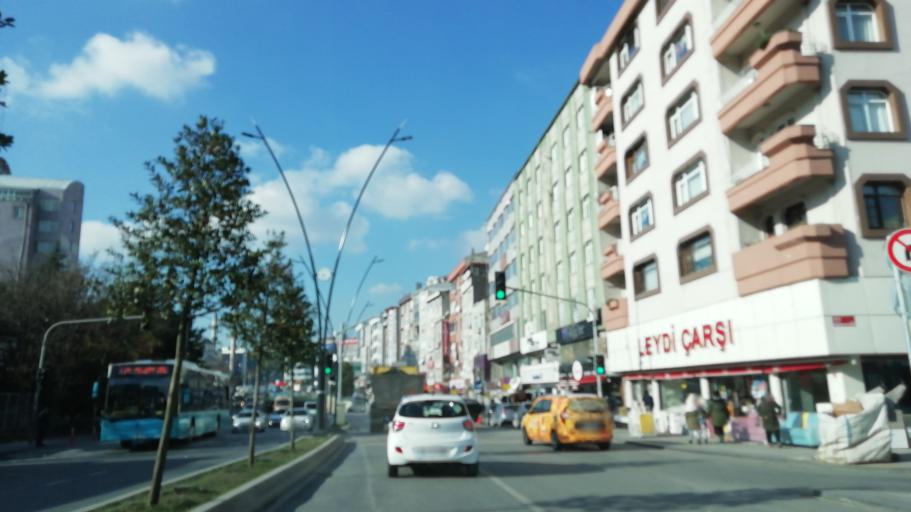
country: TR
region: Istanbul
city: Esenler
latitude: 41.0581
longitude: 28.9166
